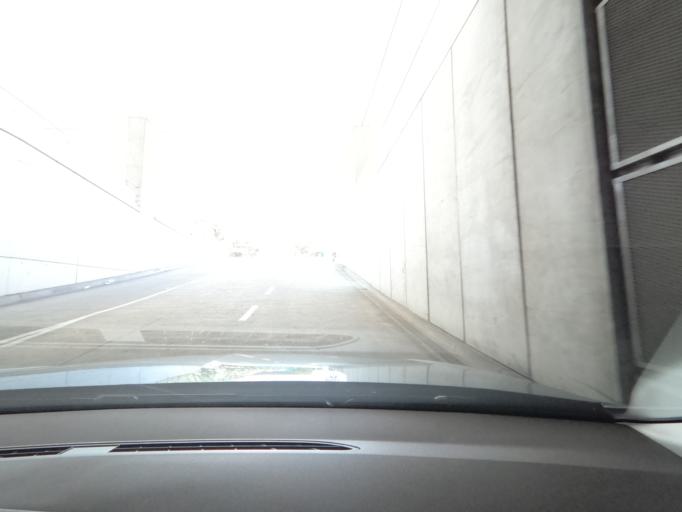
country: PT
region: Lisbon
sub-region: Loures
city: Moscavide
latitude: 38.7663
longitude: -9.0969
